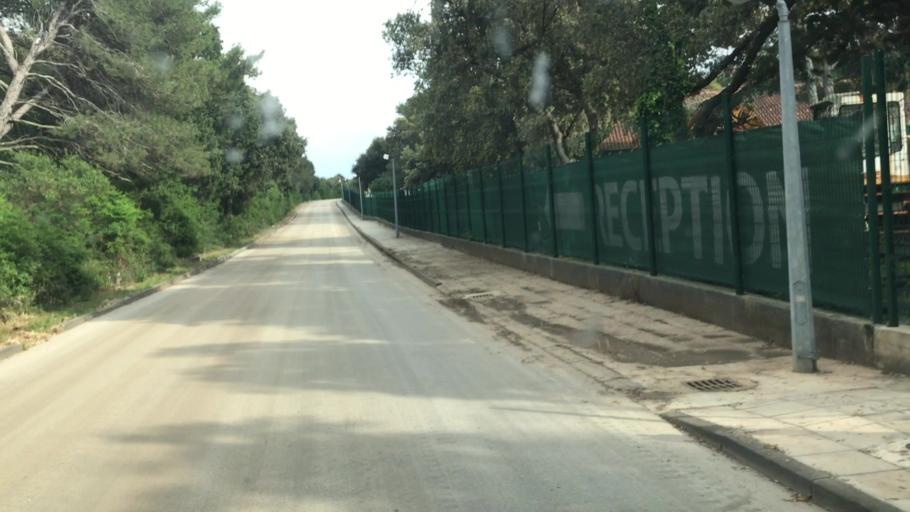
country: HR
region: Licko-Senjska
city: Novalja
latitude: 44.5450
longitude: 14.8813
